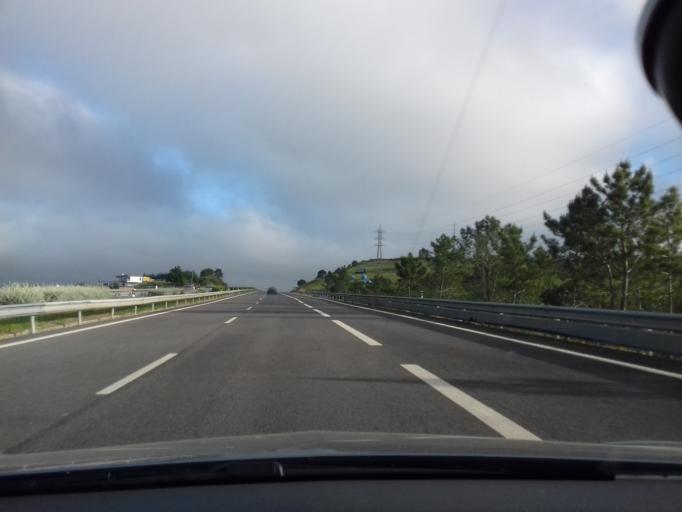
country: PT
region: Lisbon
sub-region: Mafra
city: Milharado
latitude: 38.9476
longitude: -9.2105
